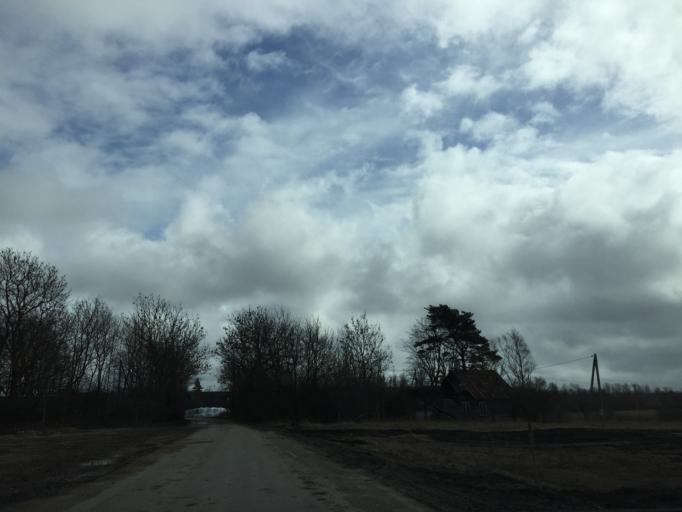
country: EE
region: Laeaene
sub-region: Lihula vald
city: Lihula
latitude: 58.7337
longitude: 23.8623
